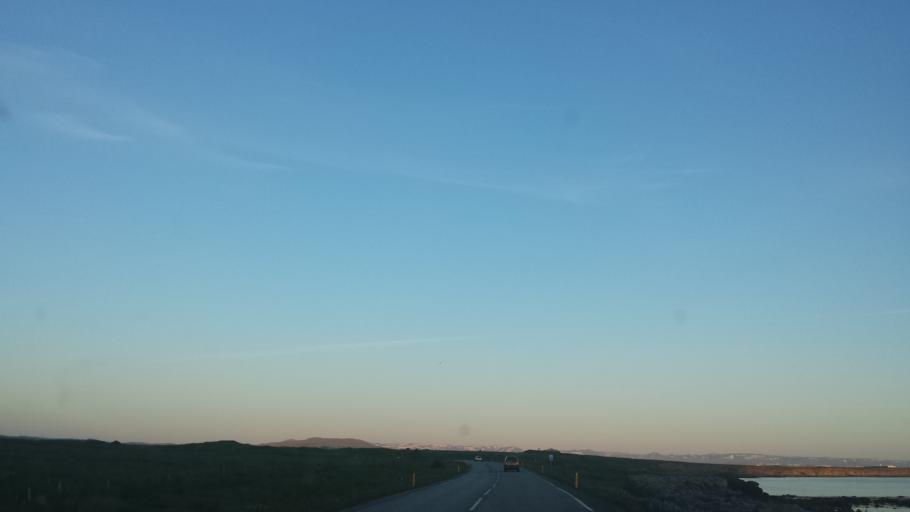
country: IS
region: Capital Region
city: Reykjavik
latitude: 64.2289
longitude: -21.8153
